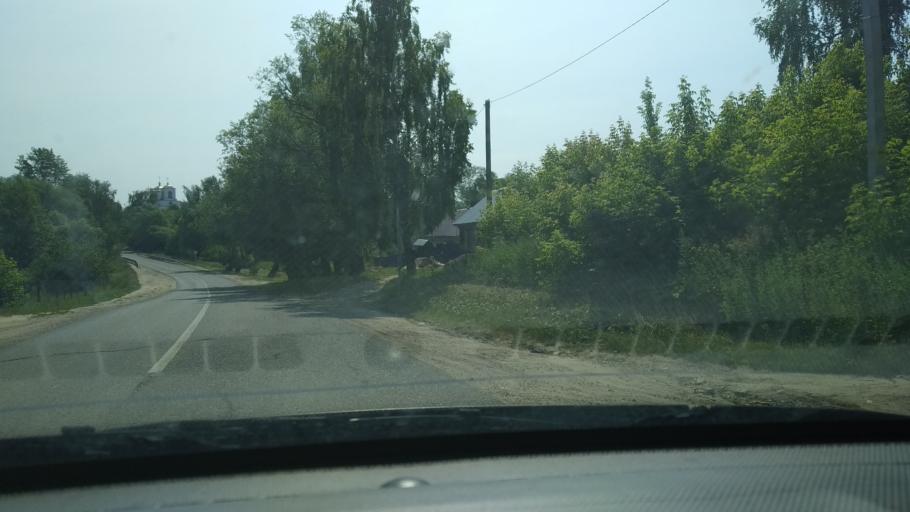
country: RU
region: Tatarstan
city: Osinovo
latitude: 55.9822
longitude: 48.7971
